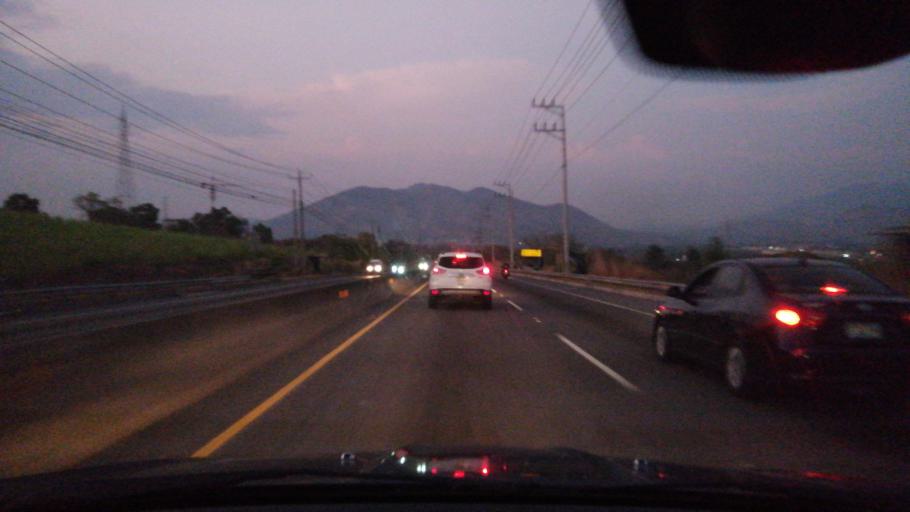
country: SV
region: San Salvador
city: Ayutuxtepeque
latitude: 13.7654
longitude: -89.2129
